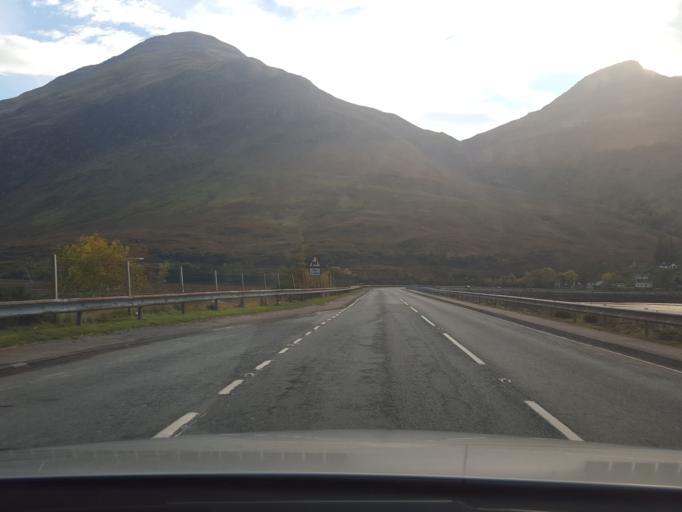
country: GB
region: Scotland
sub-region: Highland
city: Fort William
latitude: 57.2331
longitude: -5.4054
